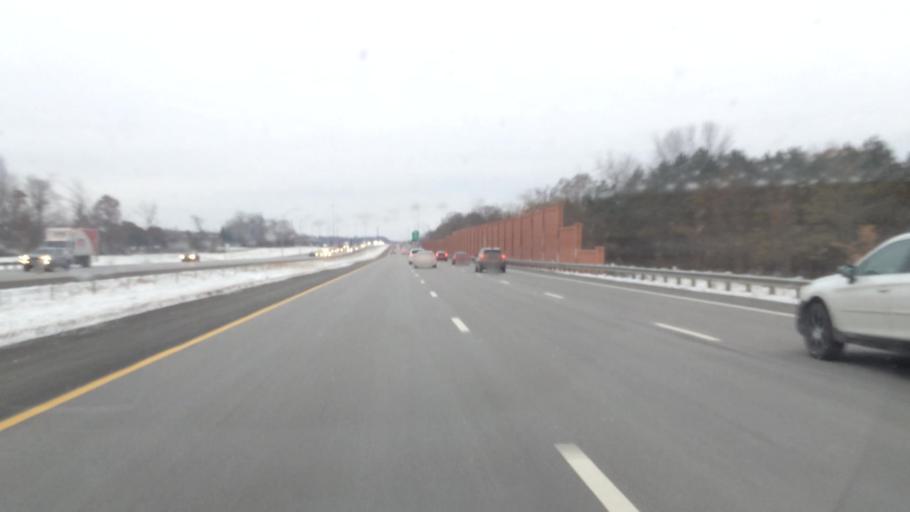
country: US
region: Ohio
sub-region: Medina County
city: Brunswick
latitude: 41.2473
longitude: -81.8015
